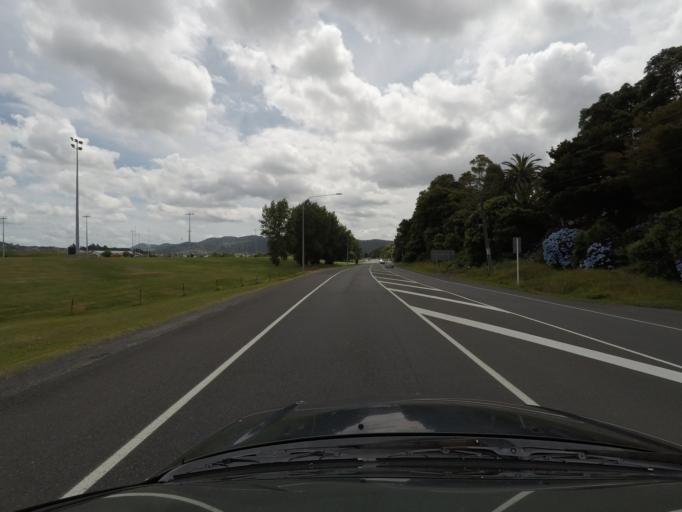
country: NZ
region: Northland
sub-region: Whangarei
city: Whangarei
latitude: -35.7307
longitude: 174.3416
